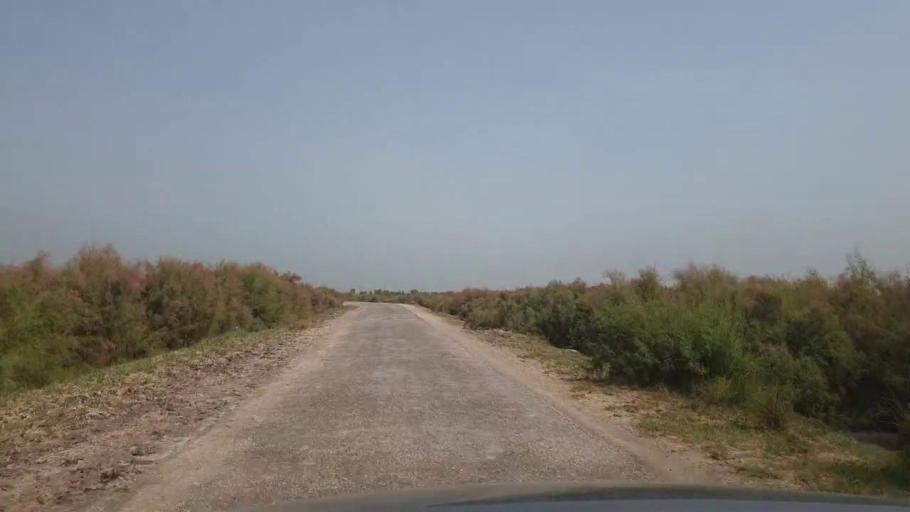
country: PK
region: Sindh
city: Madeji
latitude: 27.8317
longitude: 68.4469
